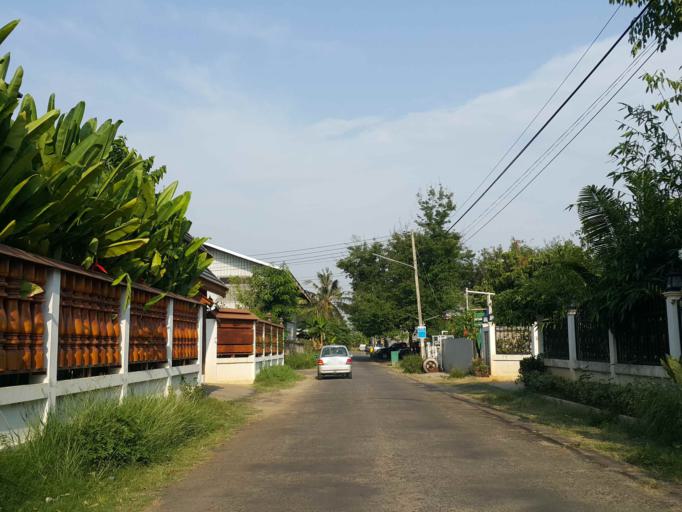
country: TH
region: Chiang Mai
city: Chiang Mai
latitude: 18.7749
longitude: 99.0235
